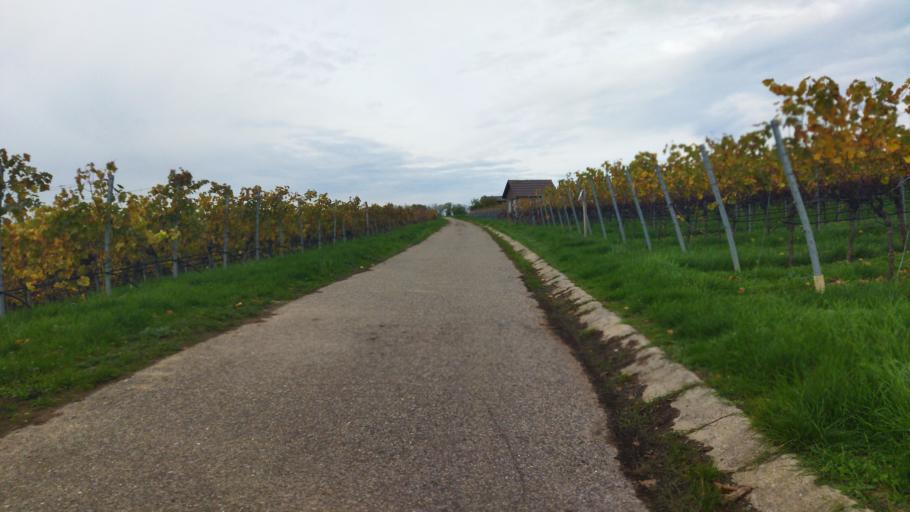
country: DE
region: Baden-Wuerttemberg
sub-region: Regierungsbezirk Stuttgart
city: Gemmrigheim
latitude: 49.0363
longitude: 9.1584
